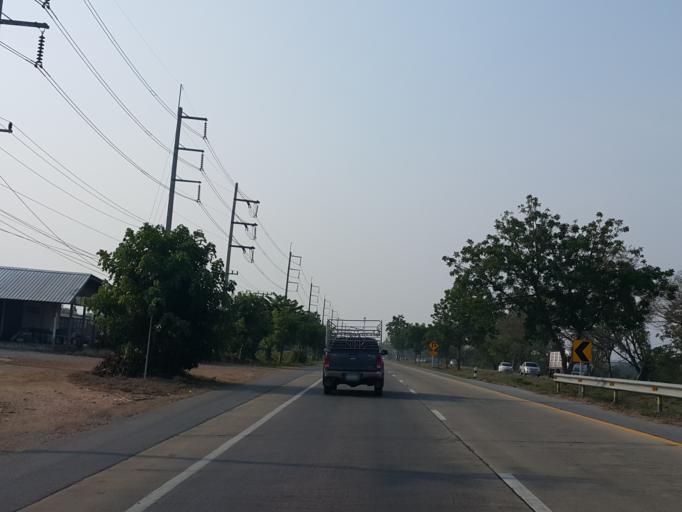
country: TH
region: Suphan Buri
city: Doem Bang Nang Buat
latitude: 14.9251
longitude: 100.0857
